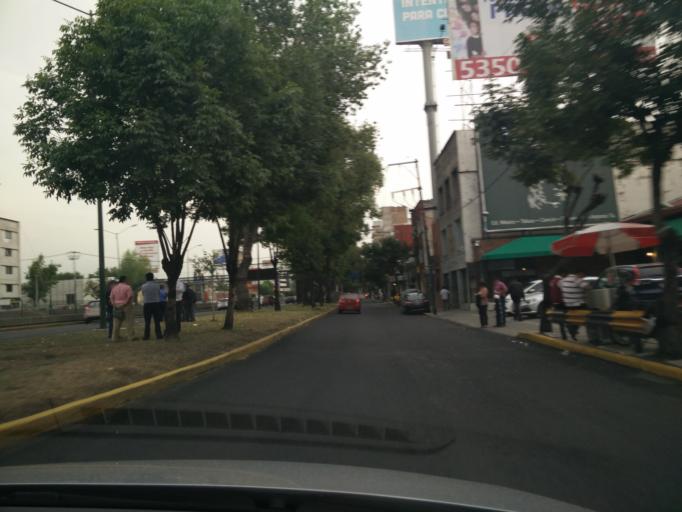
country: MX
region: Mexico City
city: Benito Juarez
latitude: 19.4039
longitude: -99.1485
